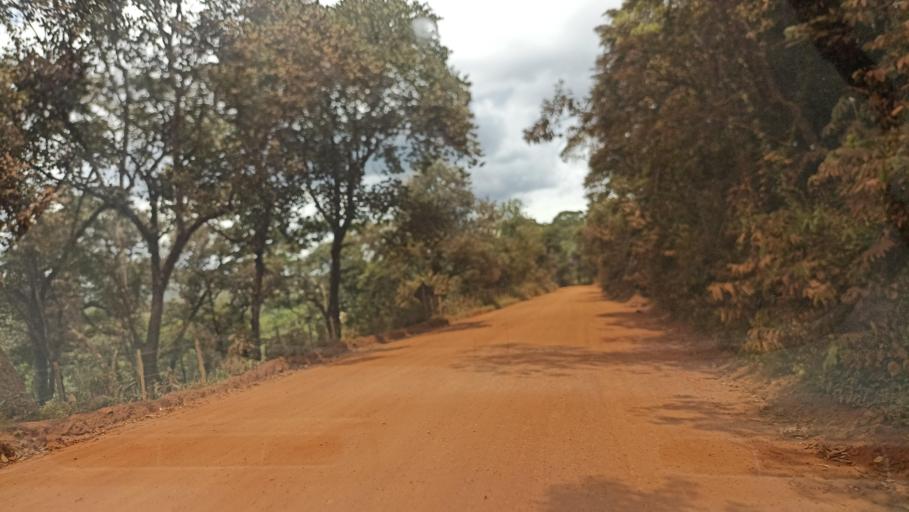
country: BR
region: Minas Gerais
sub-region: Itabirito
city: Itabirito
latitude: -20.3433
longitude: -43.7714
